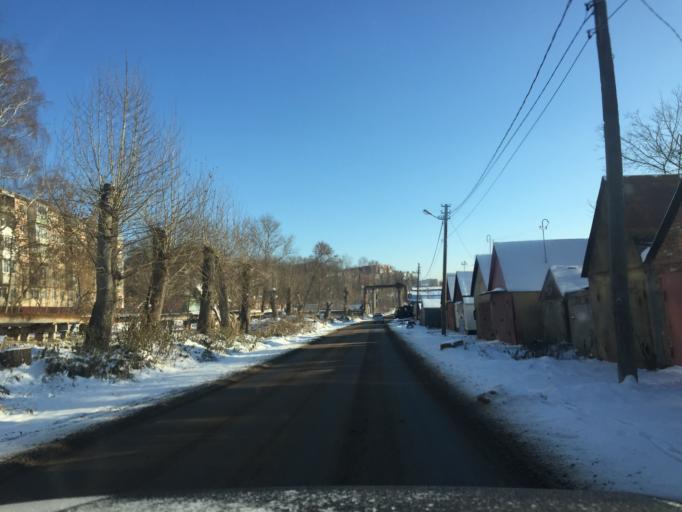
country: RU
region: Tula
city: Tula
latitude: 54.1916
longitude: 37.6768
